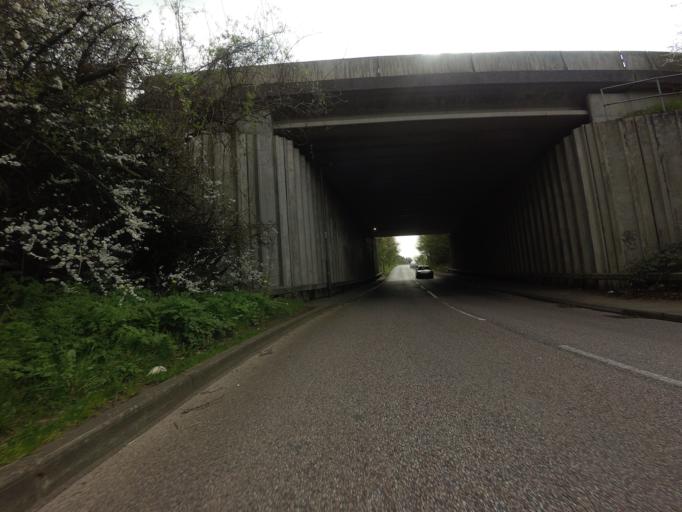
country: GB
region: England
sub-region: Greater London
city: Sidcup
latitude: 51.4108
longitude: 0.1255
